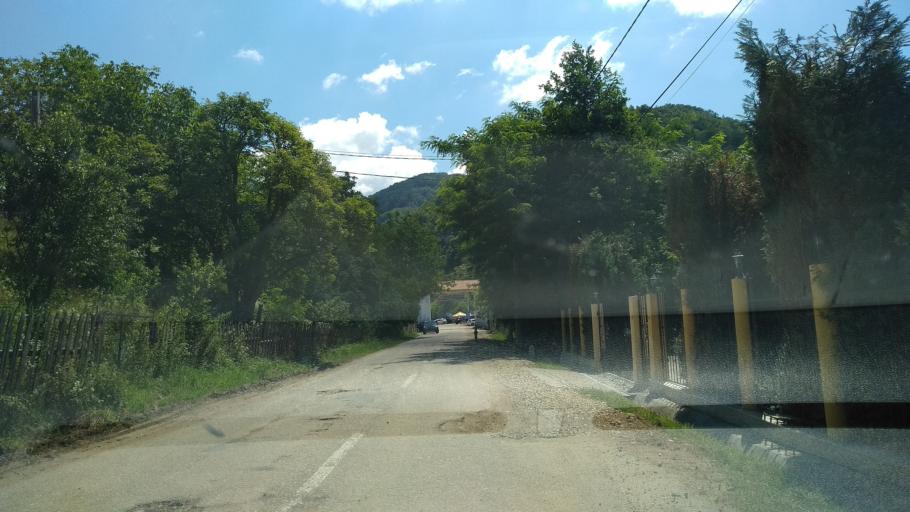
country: RO
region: Hunedoara
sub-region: Comuna Orastioara de Sus
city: Orastioara de Sus
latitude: 45.6815
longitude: 23.1618
